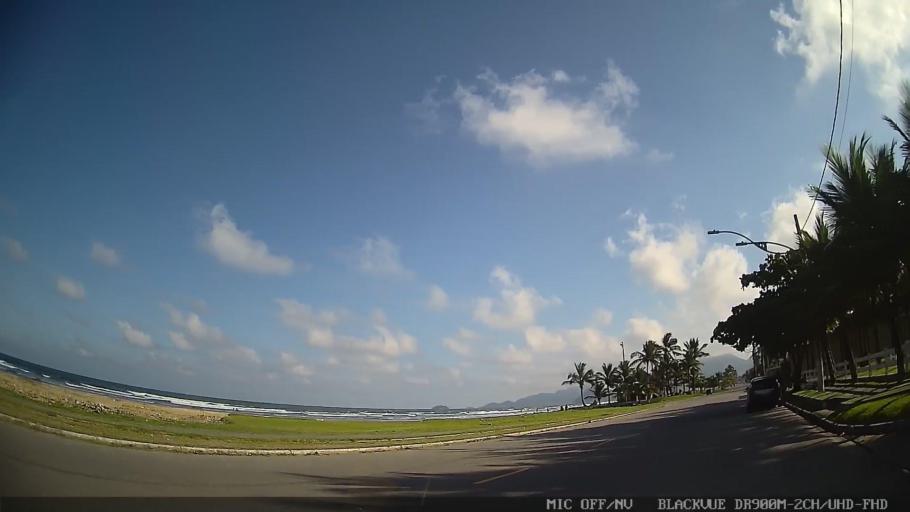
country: BR
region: Sao Paulo
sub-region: Peruibe
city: Peruibe
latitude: -24.2942
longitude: -46.9608
